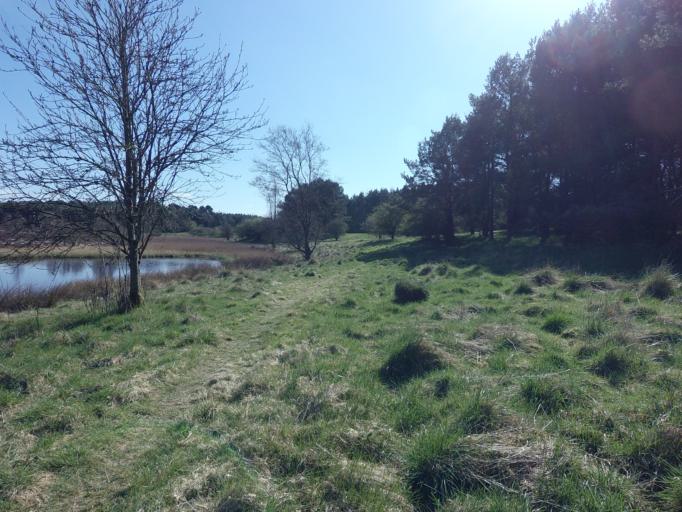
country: GB
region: Scotland
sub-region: West Lothian
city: Blackburn
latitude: 55.8936
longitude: -3.5970
